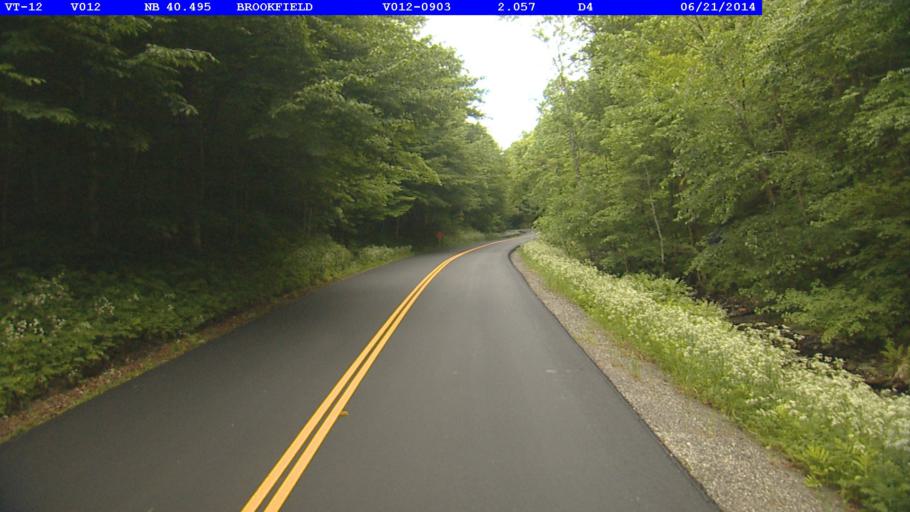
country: US
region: Vermont
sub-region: Orange County
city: Randolph
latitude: 44.0330
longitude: -72.6509
